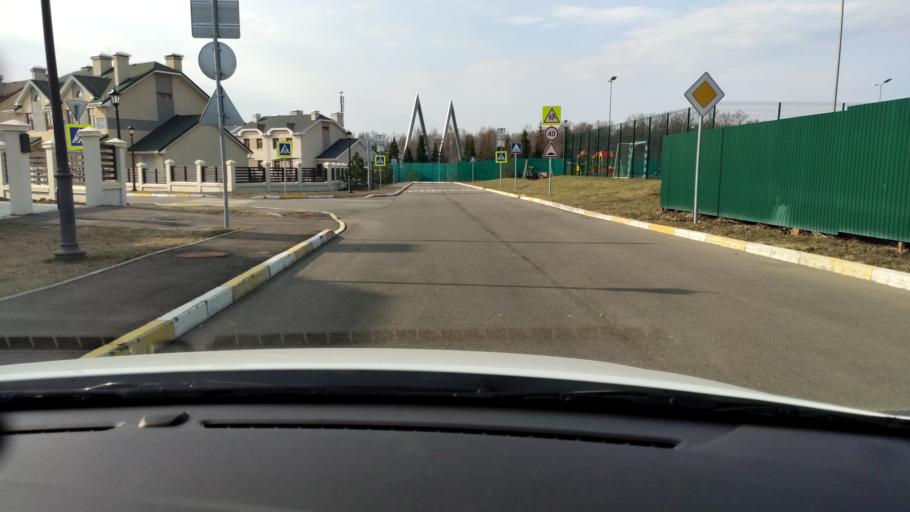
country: RU
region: Tatarstan
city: Stolbishchi
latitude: 55.7121
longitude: 49.2149
